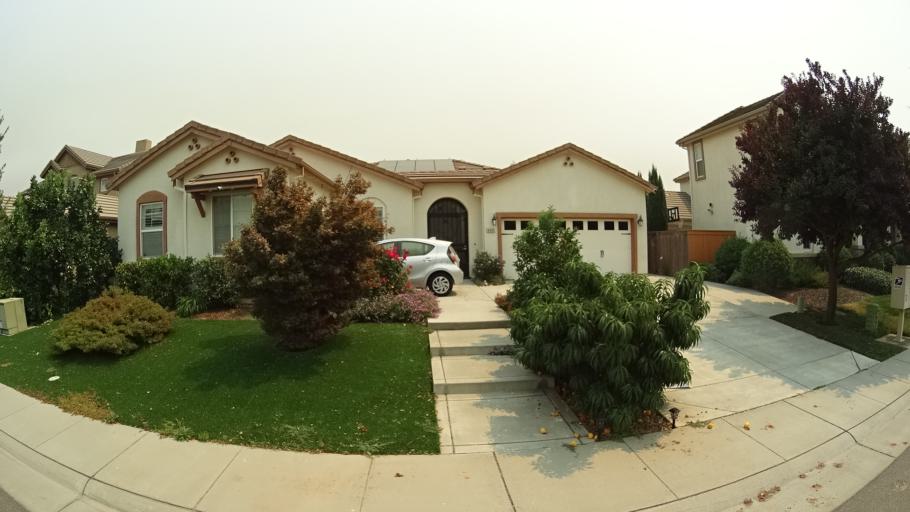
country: US
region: California
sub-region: Sacramento County
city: Laguna
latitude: 38.3958
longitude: -121.4082
